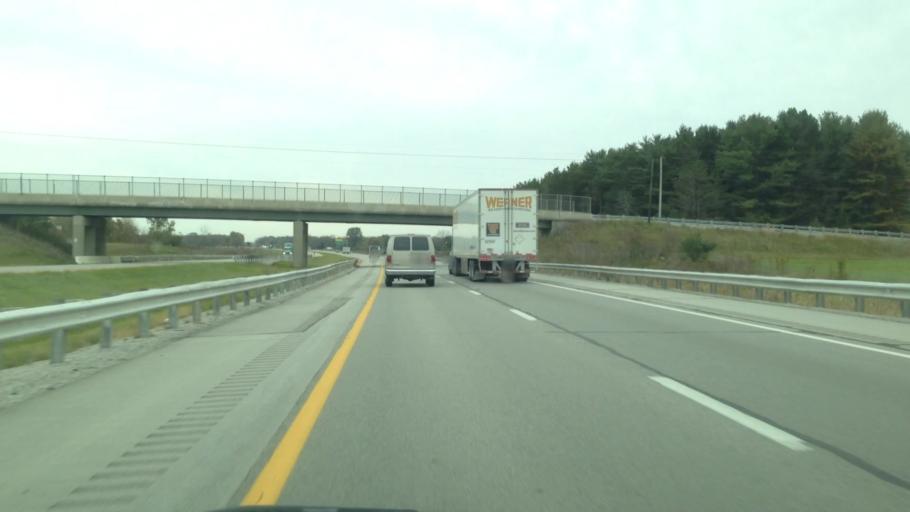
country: US
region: Ohio
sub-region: Williams County
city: Montpelier
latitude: 41.6262
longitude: -84.7070
